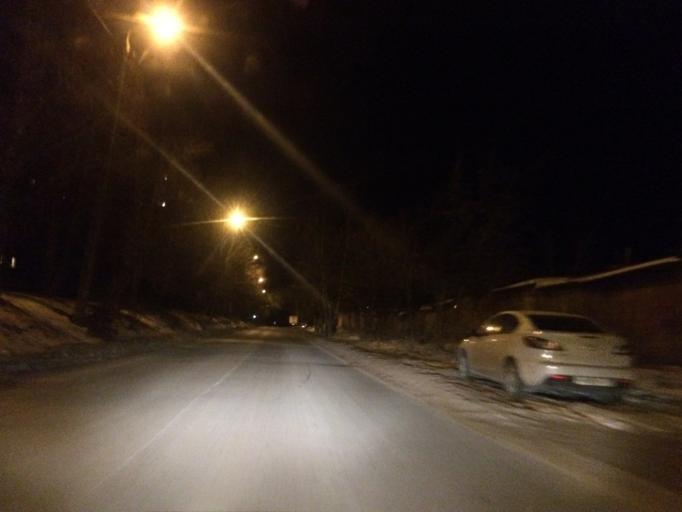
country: RU
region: Tula
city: Mendeleyevskiy
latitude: 54.1676
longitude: 37.5617
